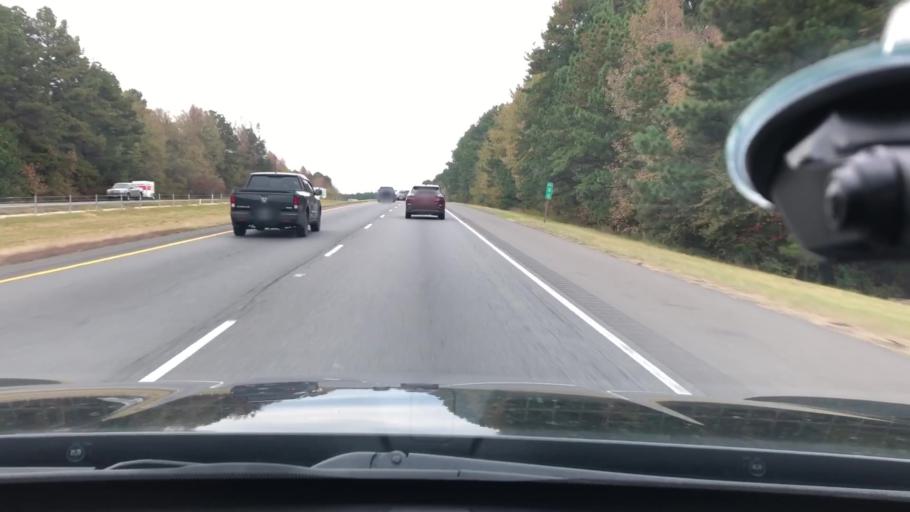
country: US
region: Arkansas
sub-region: Clark County
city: Gurdon
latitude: 34.0318
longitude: -93.1474
